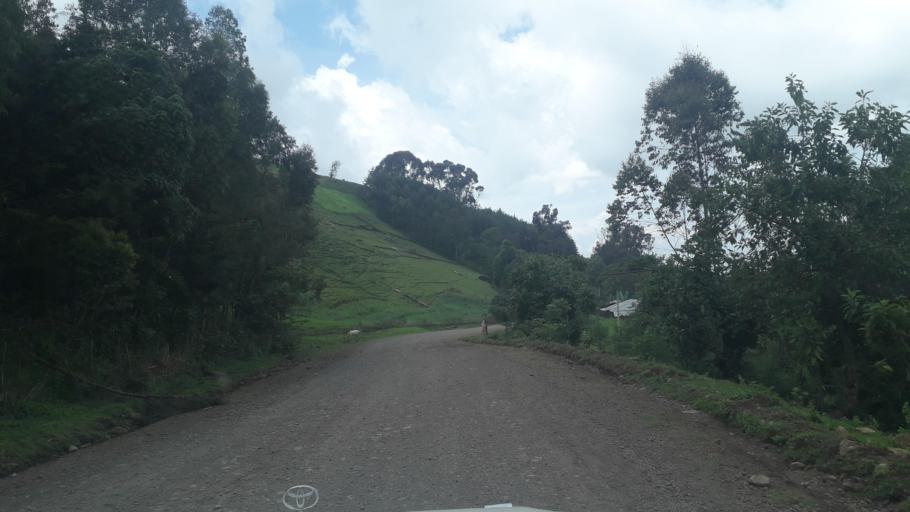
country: ET
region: Oromiya
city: Jima
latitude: 7.4477
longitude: 36.8761
